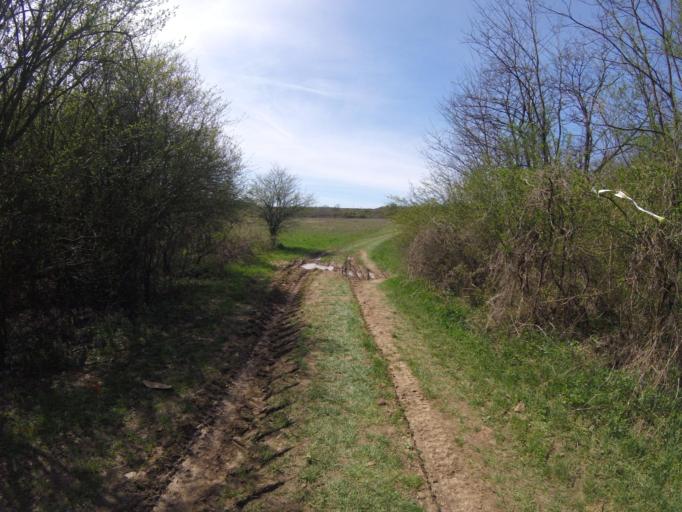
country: HU
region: Borsod-Abauj-Zemplen
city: Szendro
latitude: 48.4199
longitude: 20.7561
